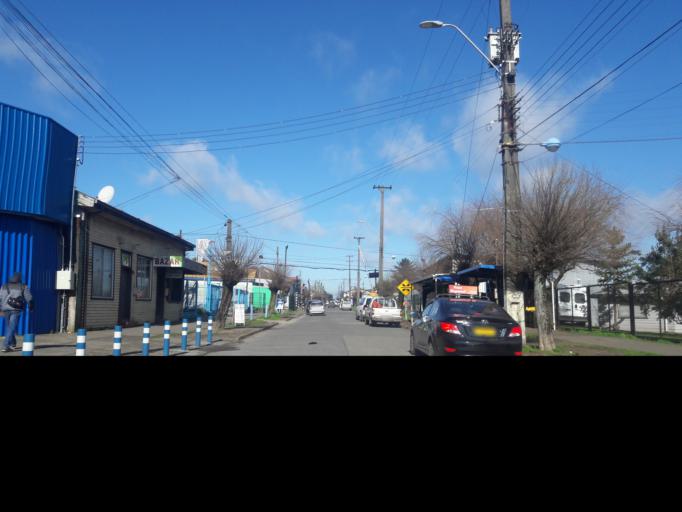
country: CL
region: Araucania
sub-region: Provincia de Malleco
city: Victoria
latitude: -38.2348
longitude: -72.3293
